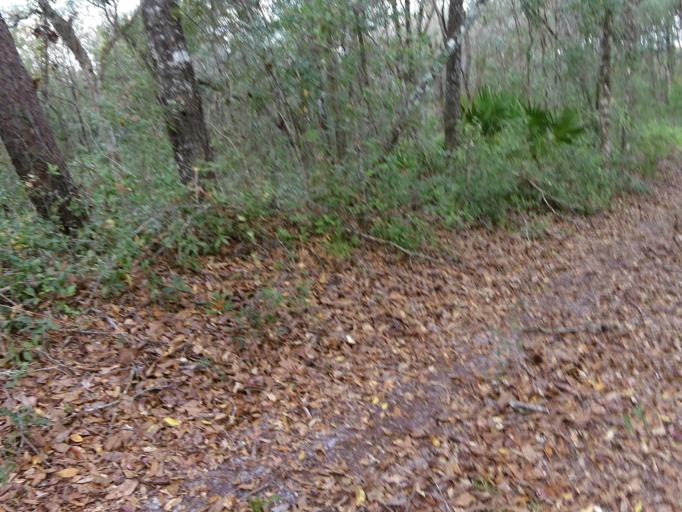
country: US
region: Florida
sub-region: Putnam County
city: Interlachen
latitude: 29.7590
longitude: -81.8206
